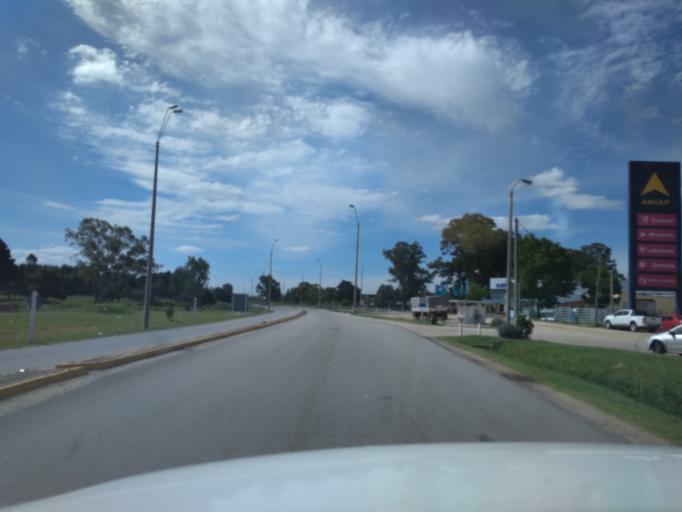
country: UY
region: Florida
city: Florida
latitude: -34.0974
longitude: -56.1966
